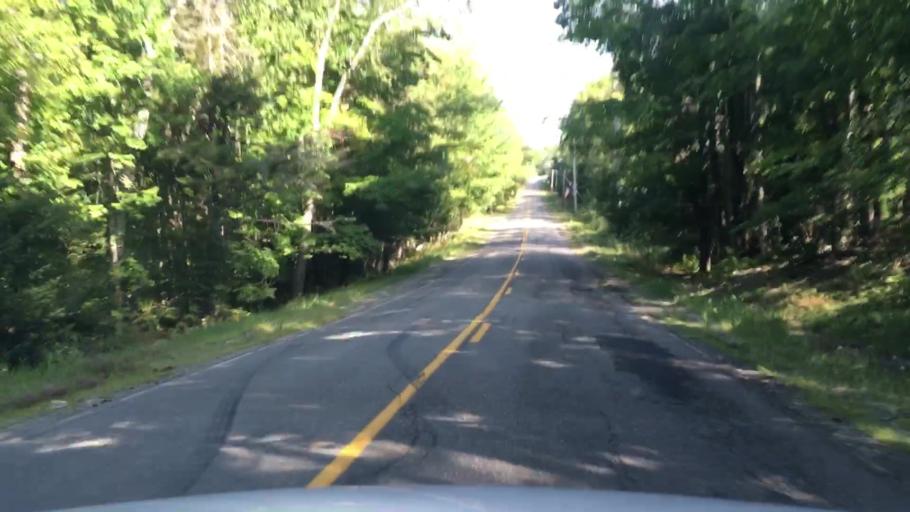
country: US
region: Maine
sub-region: Penobscot County
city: Enfield
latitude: 45.2385
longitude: -68.5520
